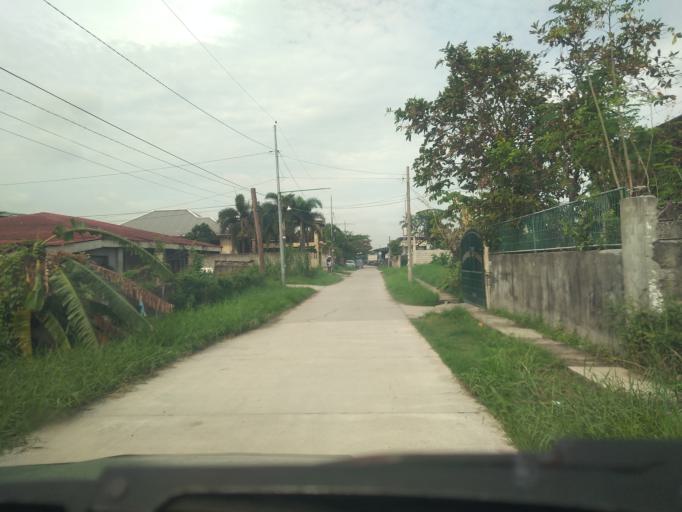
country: PH
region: Central Luzon
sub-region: Province of Pampanga
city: Pau
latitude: 15.0047
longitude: 120.7143
